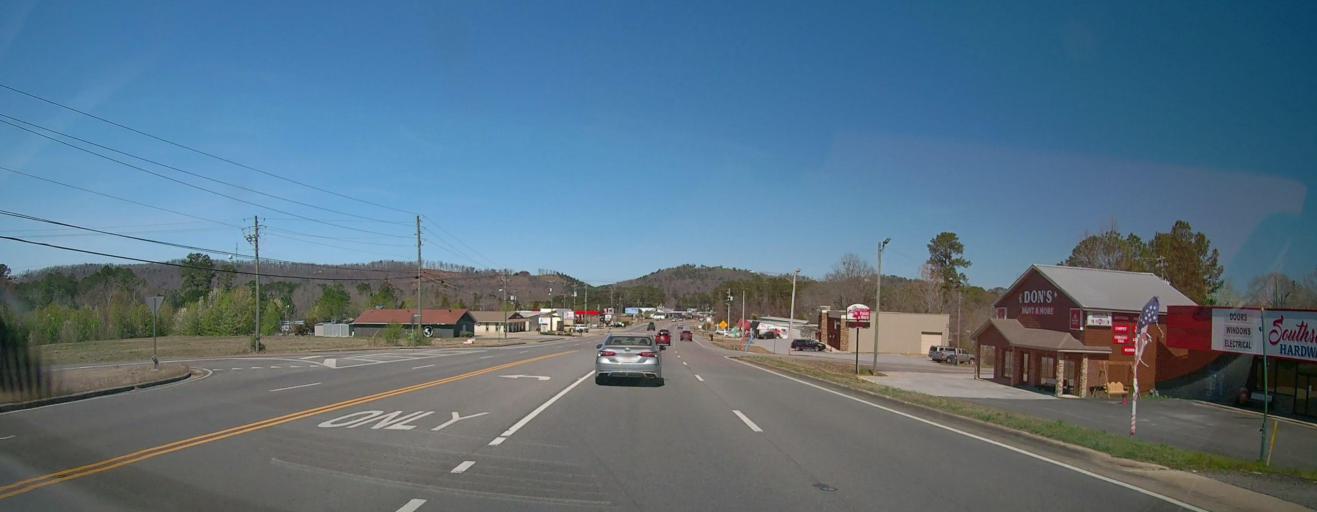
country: US
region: Alabama
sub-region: Etowah County
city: Southside
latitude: 33.9286
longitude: -86.0236
